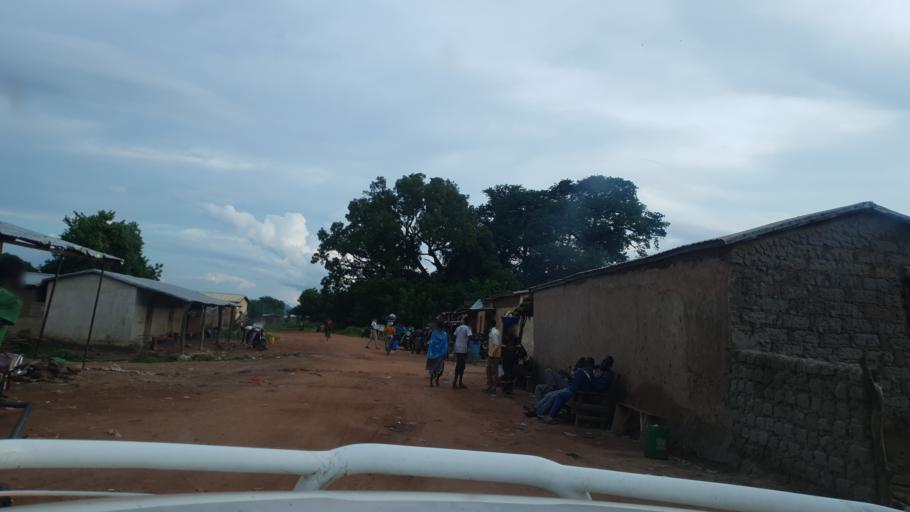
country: CI
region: Savanes
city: Tengrela
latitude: 10.5462
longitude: -6.9169
